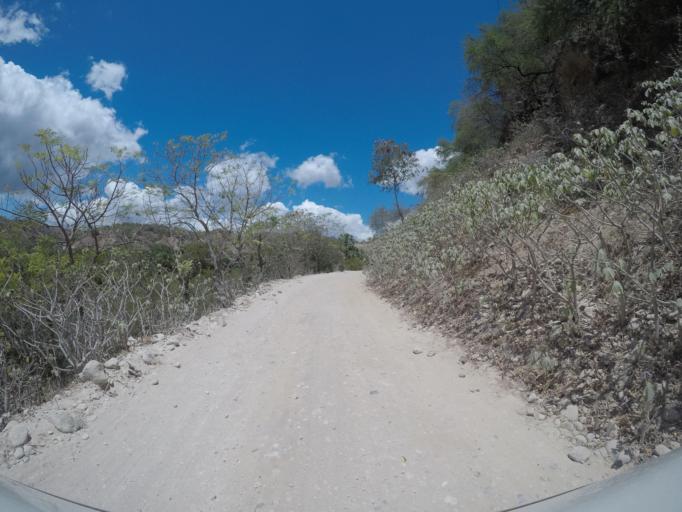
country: TL
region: Baucau
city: Baucau
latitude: -8.4728
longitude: 126.6024
